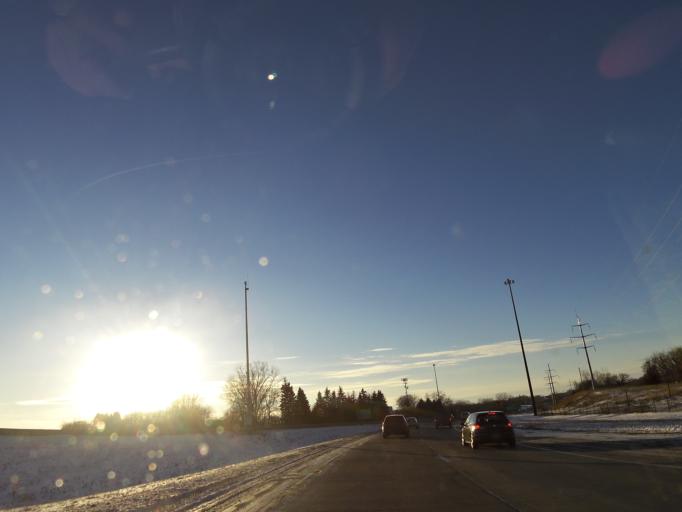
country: US
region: Minnesota
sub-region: Hennepin County
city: Eden Prairie
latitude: 44.8617
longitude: -93.4749
